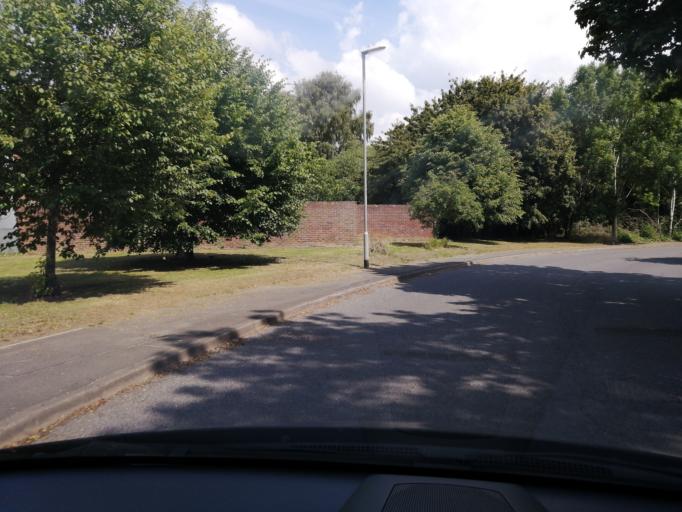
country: GB
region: England
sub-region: Cambridgeshire
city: Yaxley
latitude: 52.5204
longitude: -0.2422
